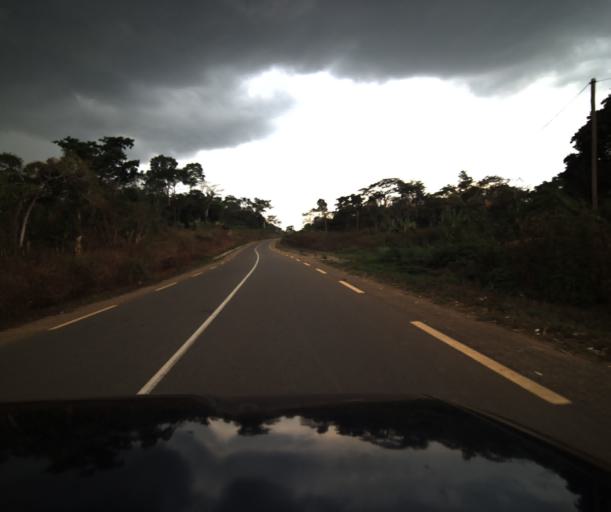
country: CM
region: Centre
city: Mbankomo
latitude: 3.6863
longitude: 11.3520
